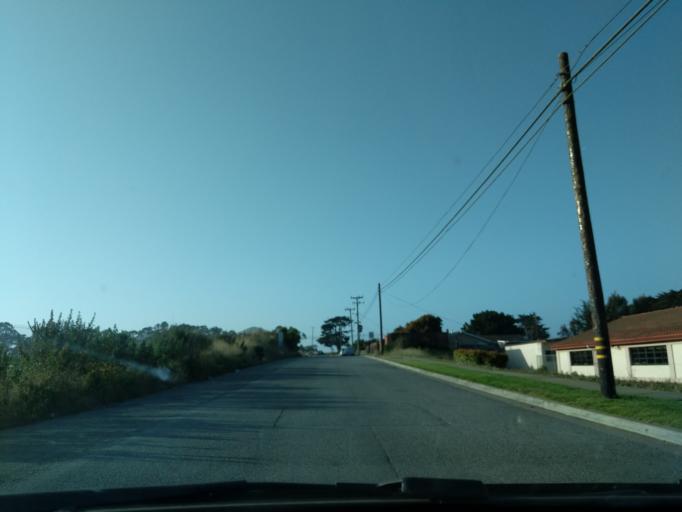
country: US
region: California
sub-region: Monterey County
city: Las Lomas
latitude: 36.8703
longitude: -121.7625
